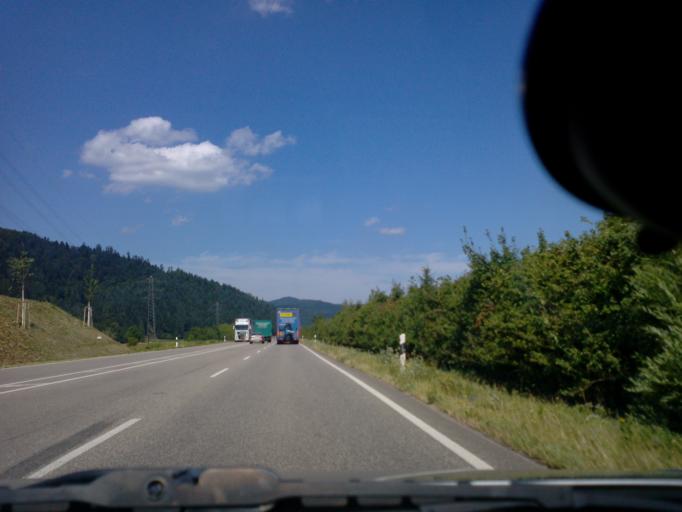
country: DE
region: Baden-Wuerttemberg
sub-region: Freiburg Region
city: Steinach
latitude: 48.3143
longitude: 8.0434
